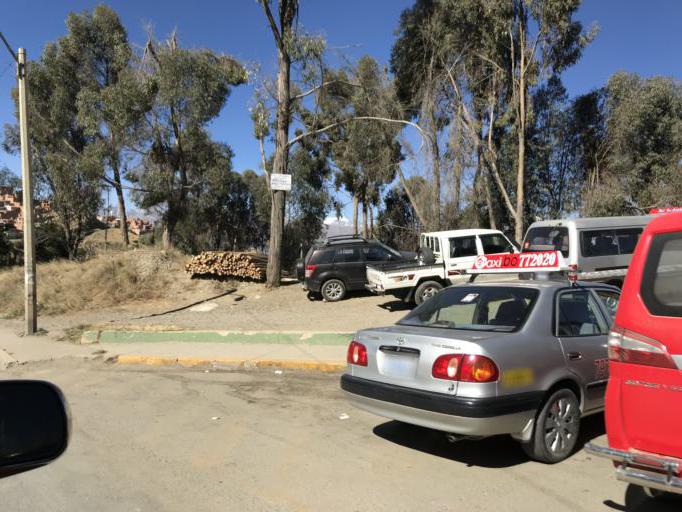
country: BO
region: La Paz
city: La Paz
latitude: -16.4859
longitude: -68.1689
